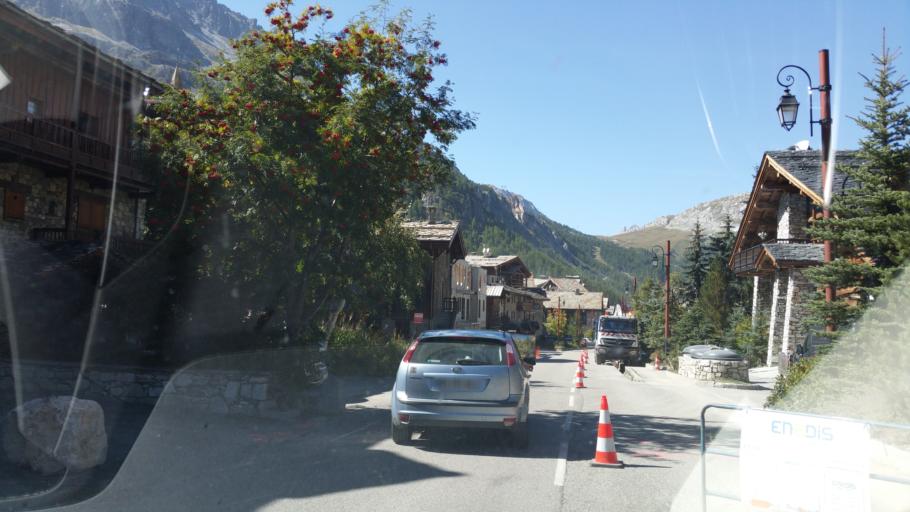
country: FR
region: Rhone-Alpes
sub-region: Departement de la Savoie
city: Val-d'Isere
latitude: 45.4479
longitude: 6.9829
